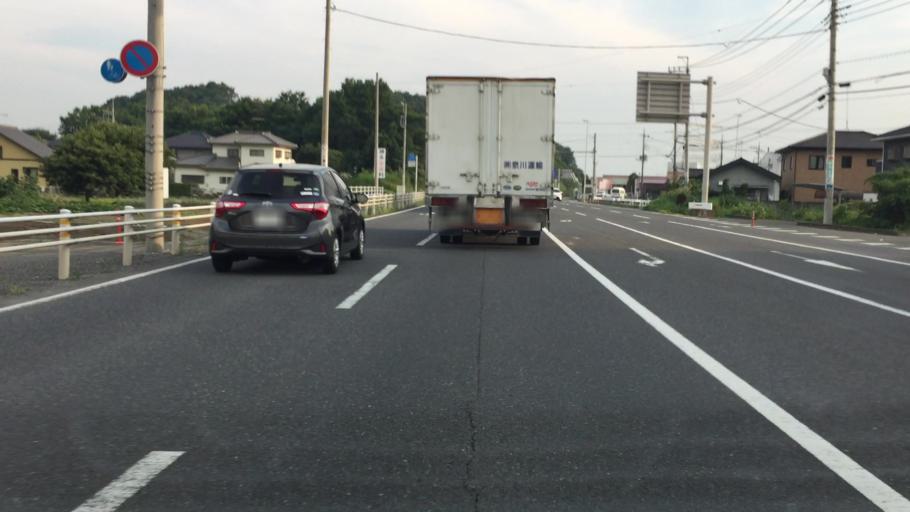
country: JP
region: Tochigi
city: Fujioka
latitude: 36.3186
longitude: 139.6764
